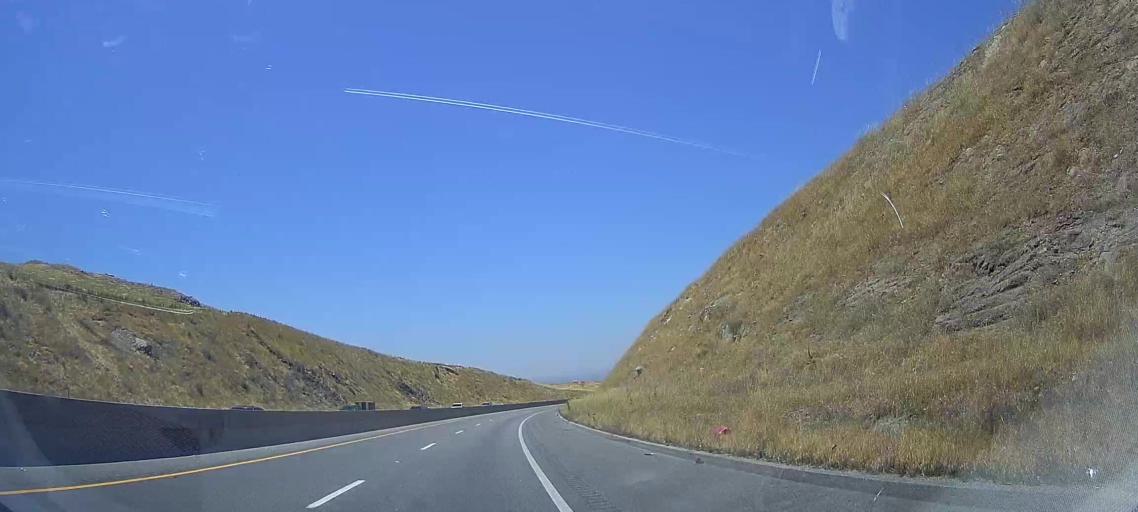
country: US
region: California
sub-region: Kern County
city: Bear Valley Springs
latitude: 35.2685
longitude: -118.6945
